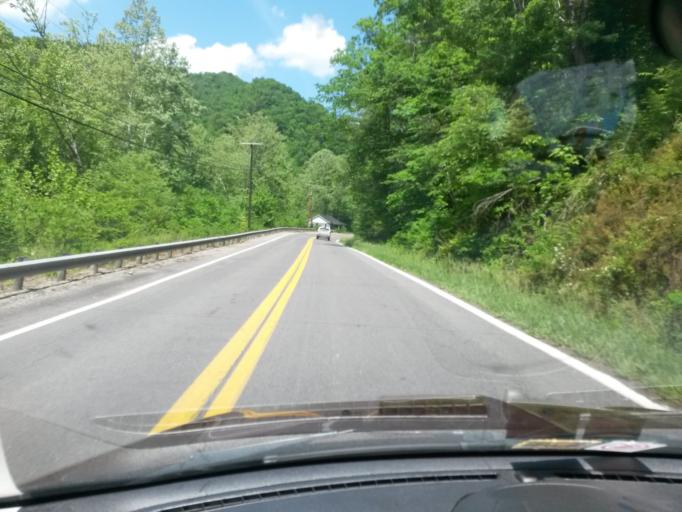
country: US
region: West Virginia
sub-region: McDowell County
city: Welch
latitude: 37.5112
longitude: -81.5765
